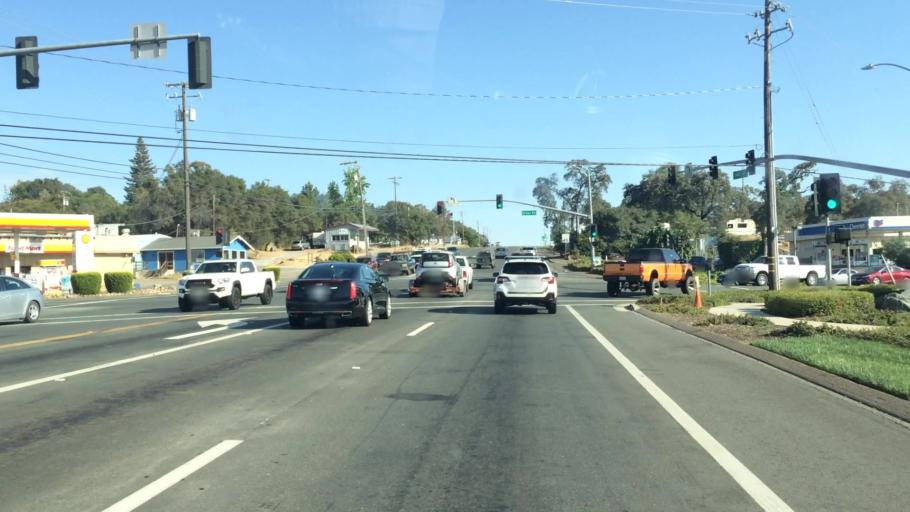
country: US
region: California
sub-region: Amador County
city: Sutter Creek
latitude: 38.3788
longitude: -120.8027
